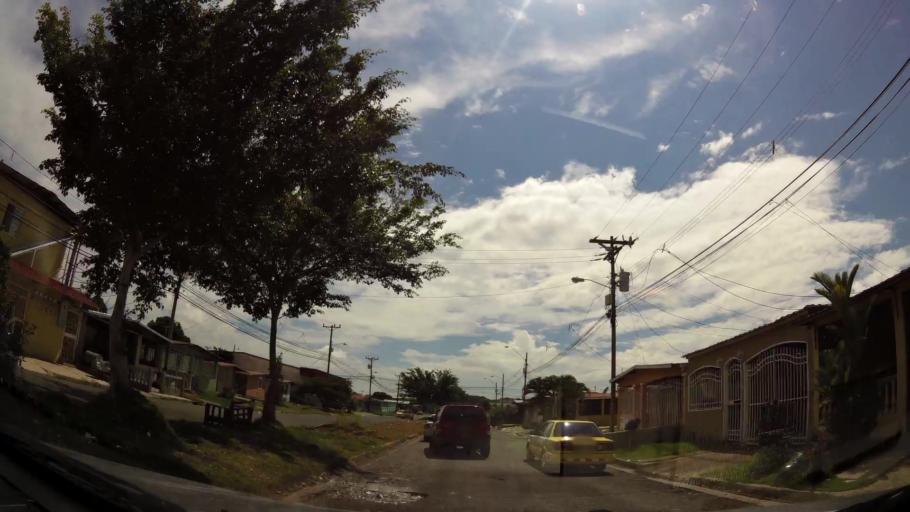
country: PA
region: Panama
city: Nuevo Arraijan
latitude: 8.9028
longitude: -79.7098
